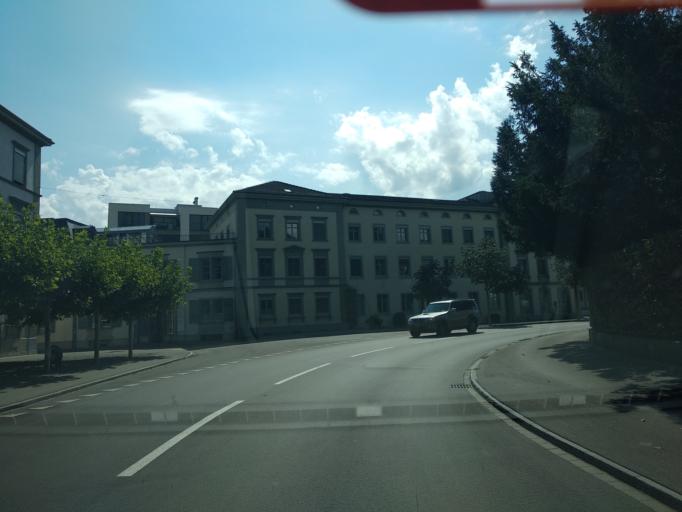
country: CH
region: Thurgau
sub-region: Frauenfeld District
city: Frauenfeld
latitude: 47.5571
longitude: 8.8991
